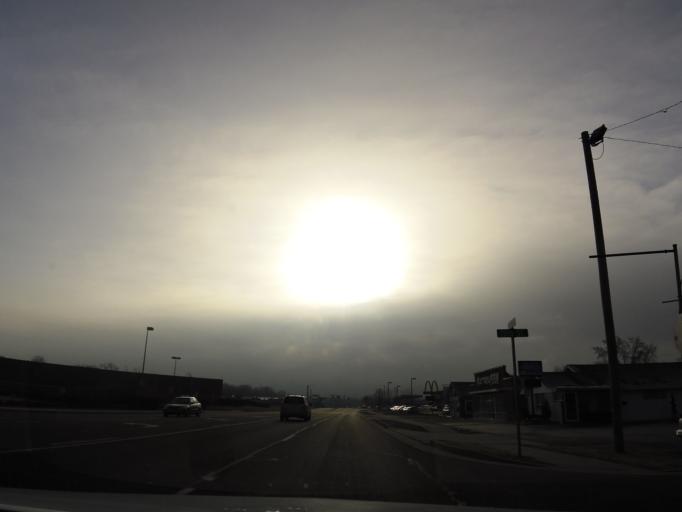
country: US
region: Indiana
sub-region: Bartholomew County
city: Columbus
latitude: 39.2192
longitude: -85.8867
